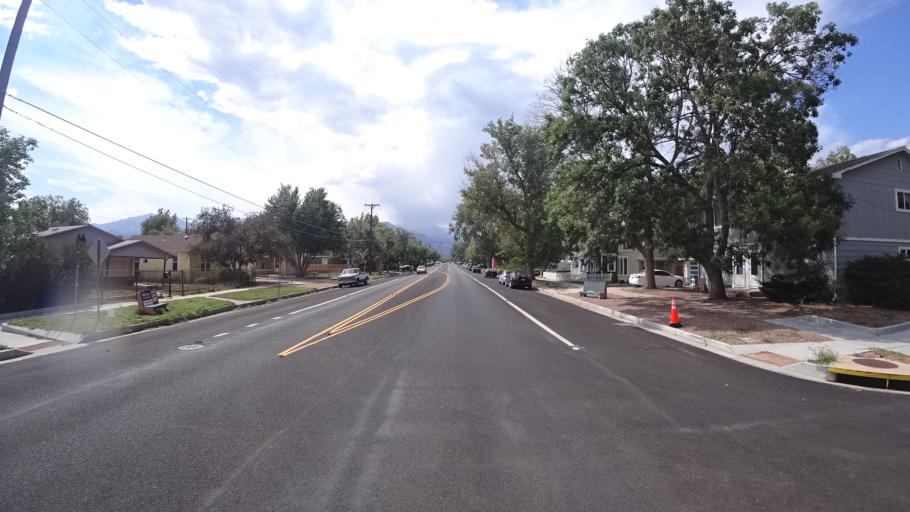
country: US
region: Colorado
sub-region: El Paso County
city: Colorado Springs
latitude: 38.8462
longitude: -104.8124
